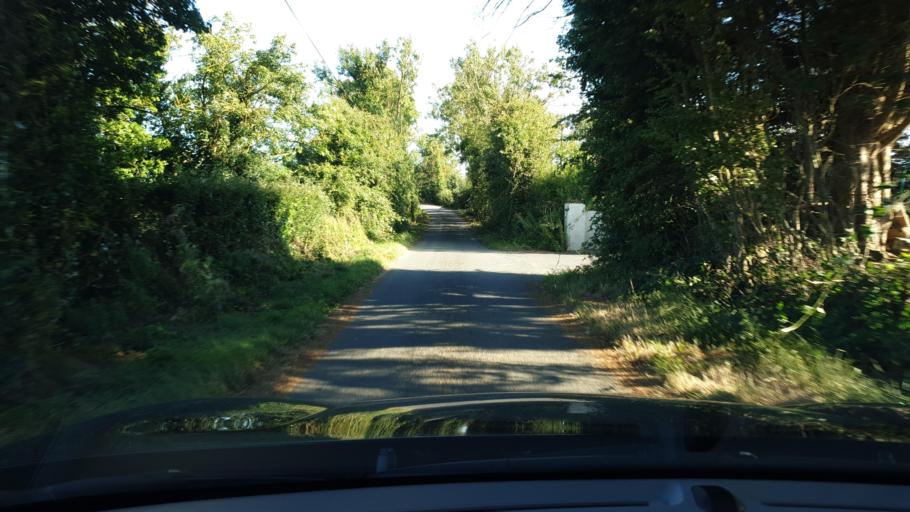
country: IE
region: Leinster
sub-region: An Mhi
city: Stamullin
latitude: 53.5917
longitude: -6.2586
